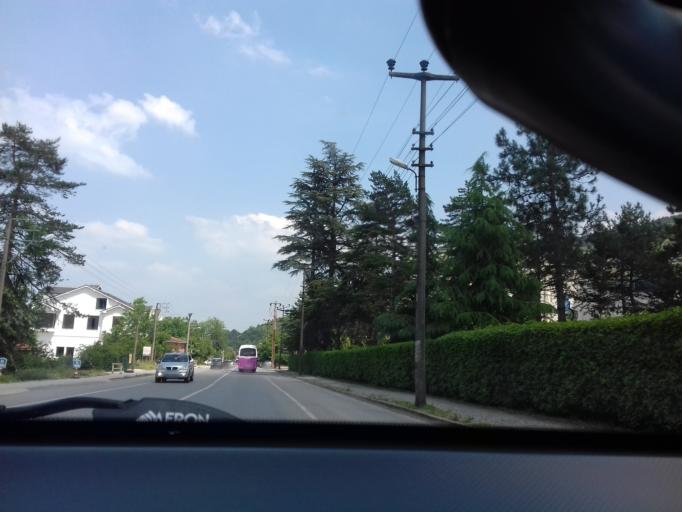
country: TR
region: Sakarya
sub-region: Merkez
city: Sapanca
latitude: 40.6913
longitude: 30.2138
